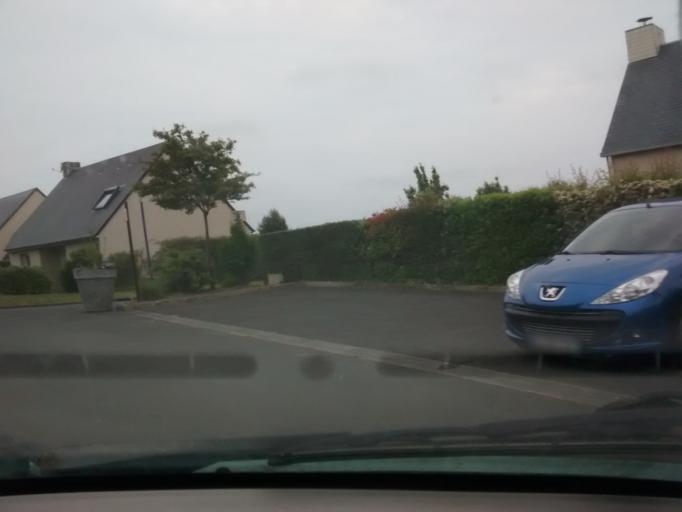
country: FR
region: Lower Normandy
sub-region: Departement de la Manche
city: Saint-Lo
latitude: 49.1046
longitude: -1.0810
